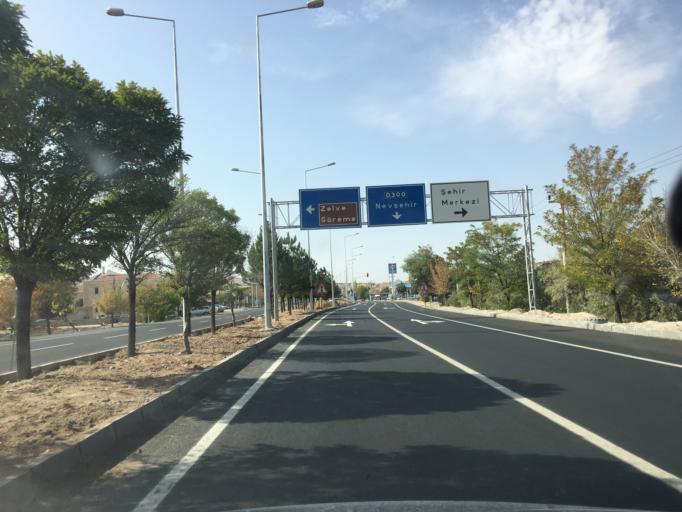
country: TR
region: Nevsehir
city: Avanos
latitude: 38.7036
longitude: 34.8449
